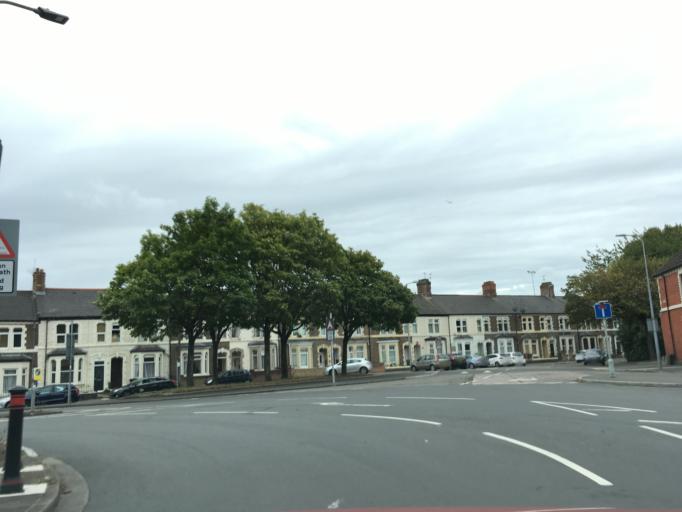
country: GB
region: Wales
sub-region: Cardiff
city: Cardiff
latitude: 51.4815
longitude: -3.1468
